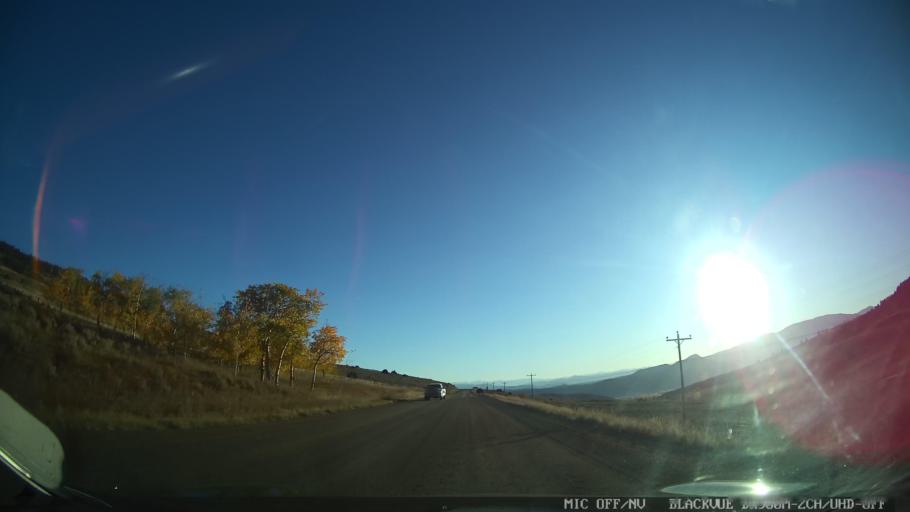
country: US
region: Colorado
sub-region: Grand County
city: Kremmling
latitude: 39.9876
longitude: -106.4298
